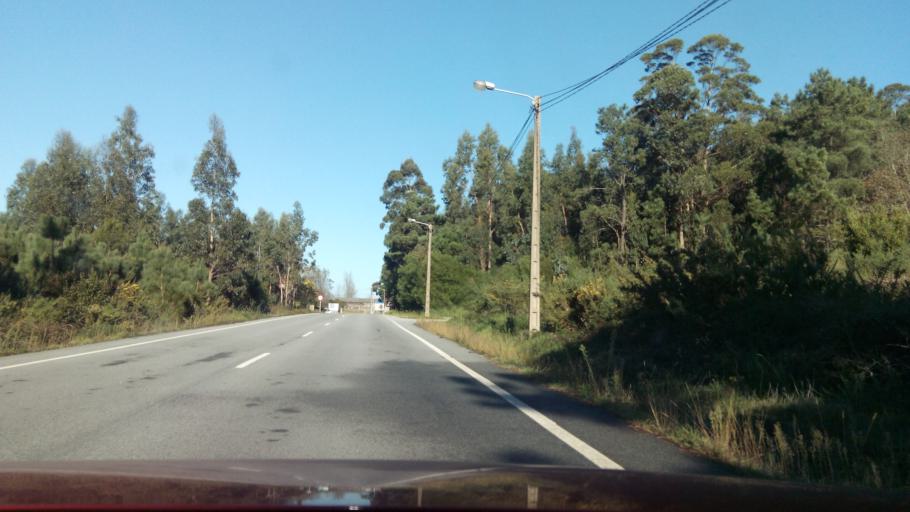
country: ES
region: Galicia
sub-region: Provincia de Pontevedra
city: O Grove
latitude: 42.4641
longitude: -8.9277
